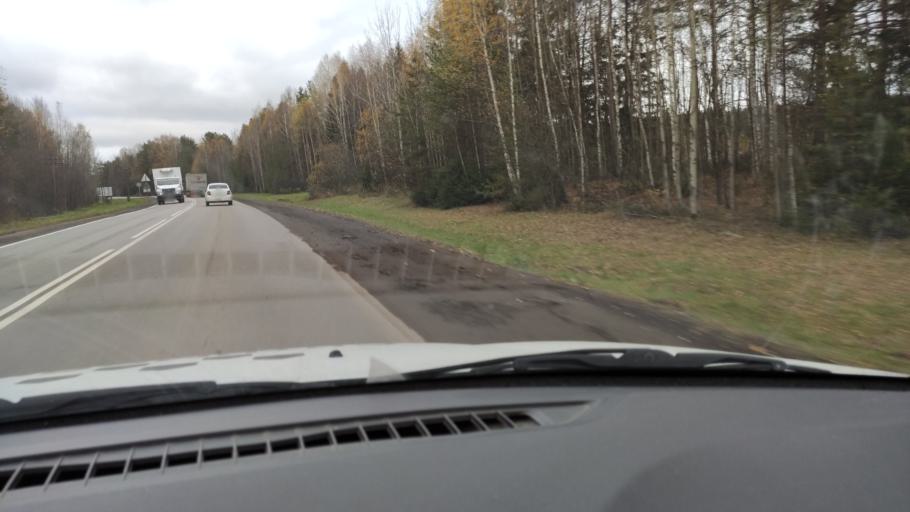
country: RU
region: Kirov
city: Slobodskoy
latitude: 58.7876
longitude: 50.5085
